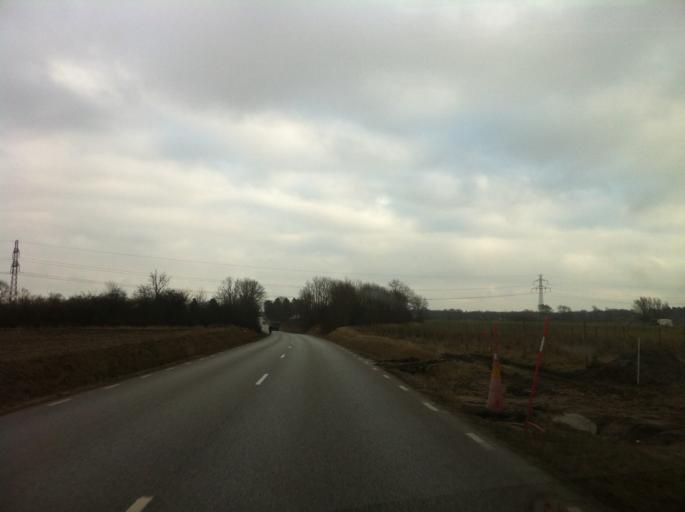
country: SE
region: Skane
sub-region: Kavlinge Kommun
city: Hofterup
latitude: 55.8238
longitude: 12.9890
